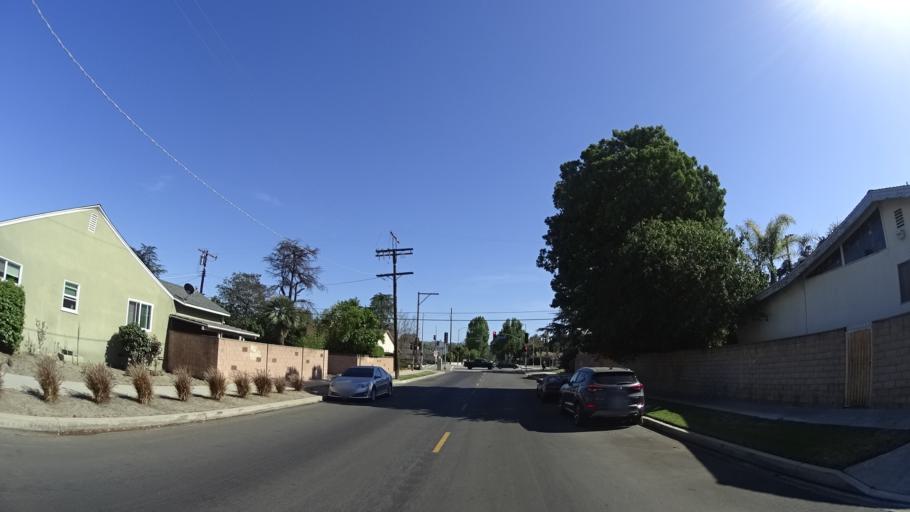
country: US
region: California
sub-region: Los Angeles County
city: North Hollywood
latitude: 34.1694
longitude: -118.4095
